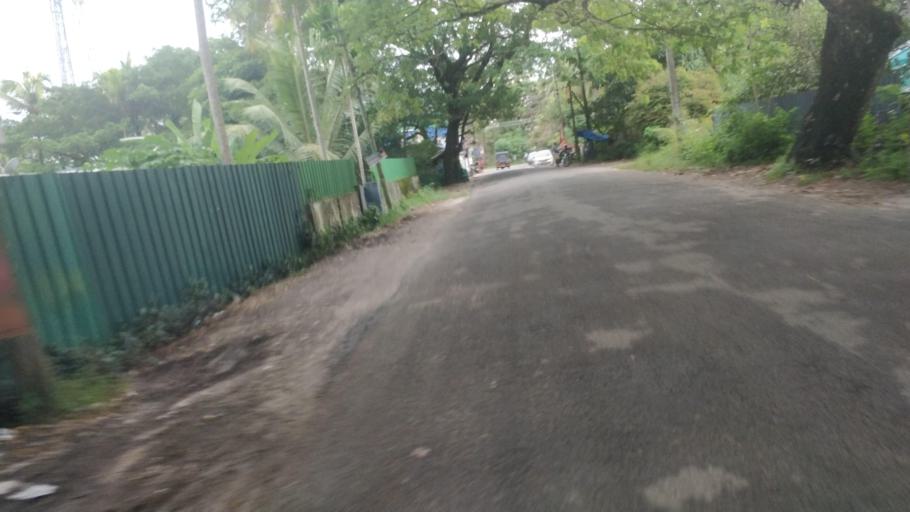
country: IN
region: Kerala
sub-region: Alappuzha
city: Shertallai
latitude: 9.6872
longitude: 76.3539
